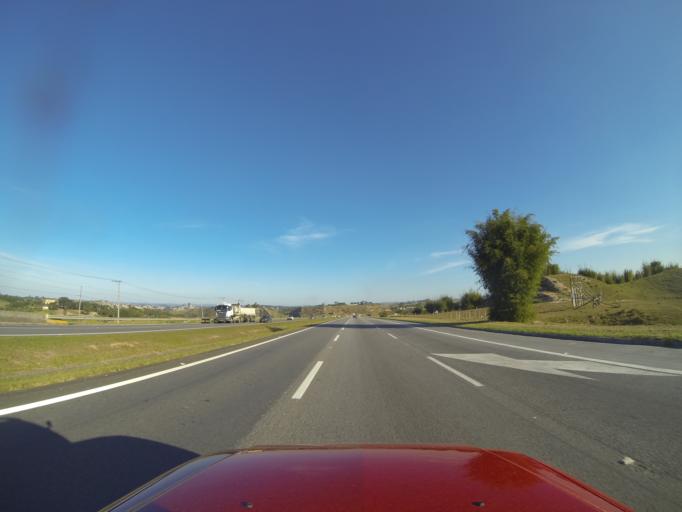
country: BR
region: Sao Paulo
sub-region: Jacarei
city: Jacarei
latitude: -23.2822
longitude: -46.0493
